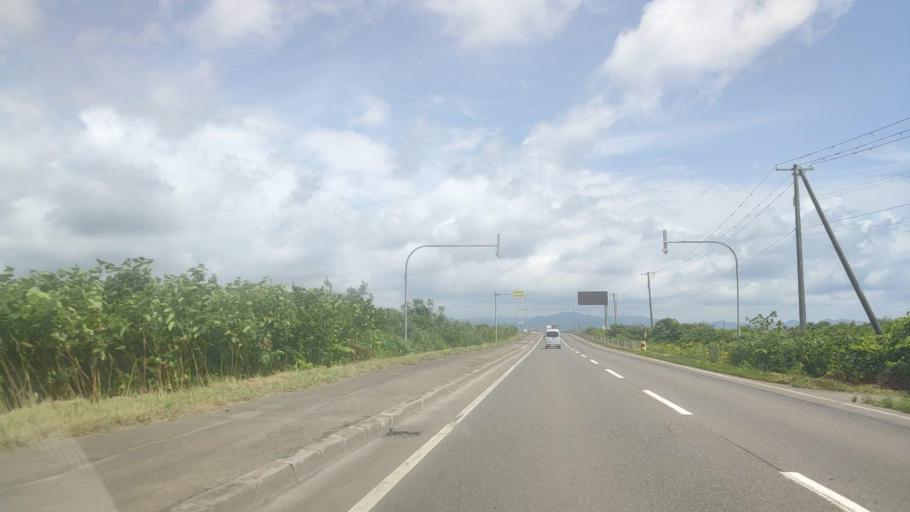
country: JP
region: Hokkaido
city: Niseko Town
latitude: 42.5223
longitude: 140.3856
